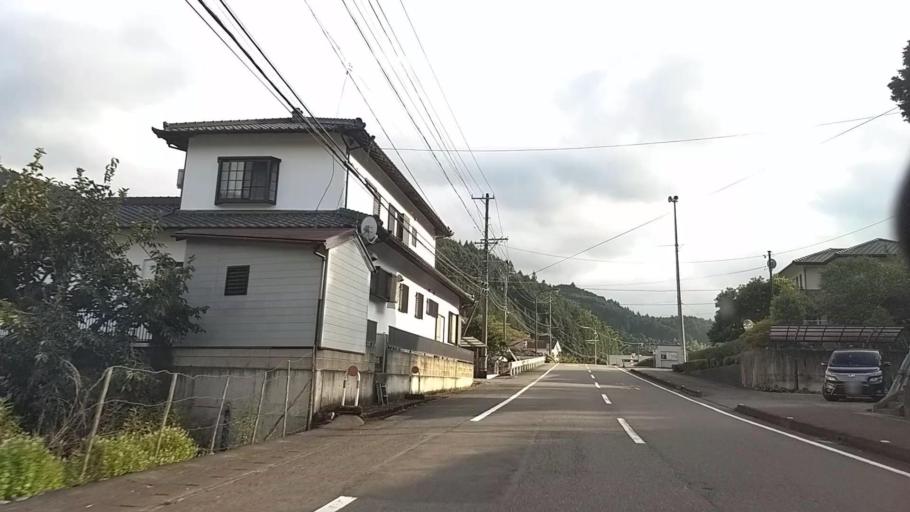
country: JP
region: Shizuoka
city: Fujinomiya
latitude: 35.1829
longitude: 138.5458
